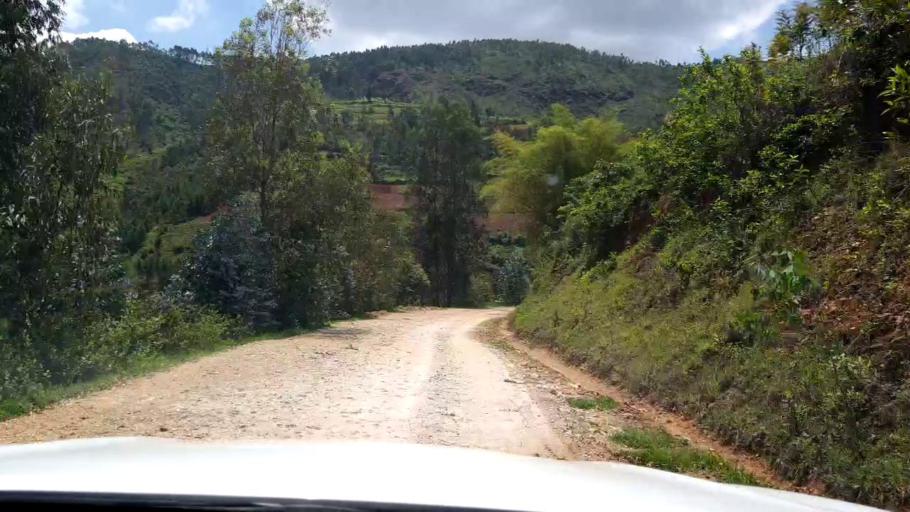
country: RW
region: Southern Province
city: Gitarama
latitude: -1.9843
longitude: 29.6226
